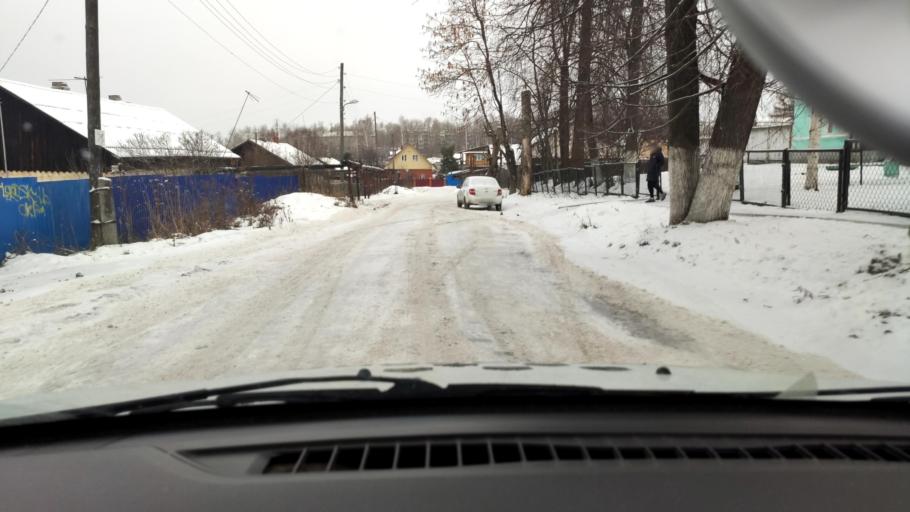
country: RU
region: Perm
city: Polazna
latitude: 58.1277
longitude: 56.3780
